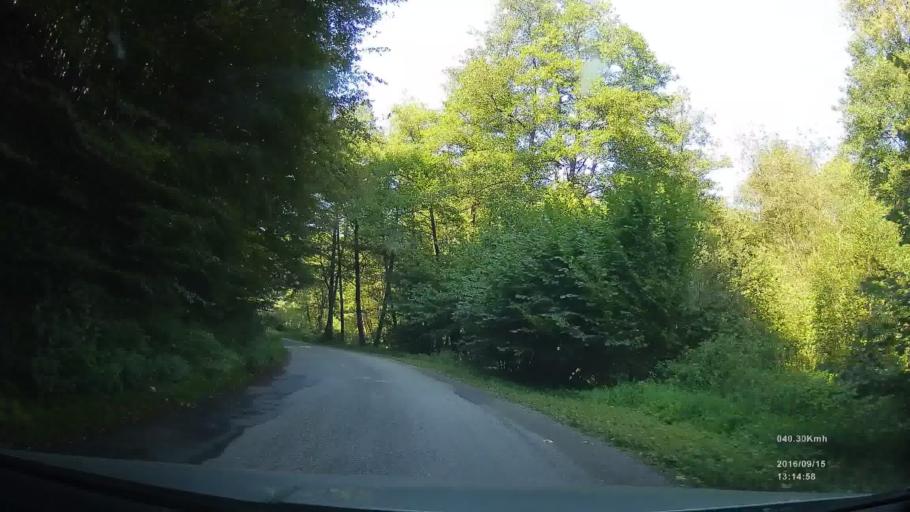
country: SK
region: Presovsky
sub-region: Okres Presov
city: Presov
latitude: 48.8942
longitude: 21.2069
